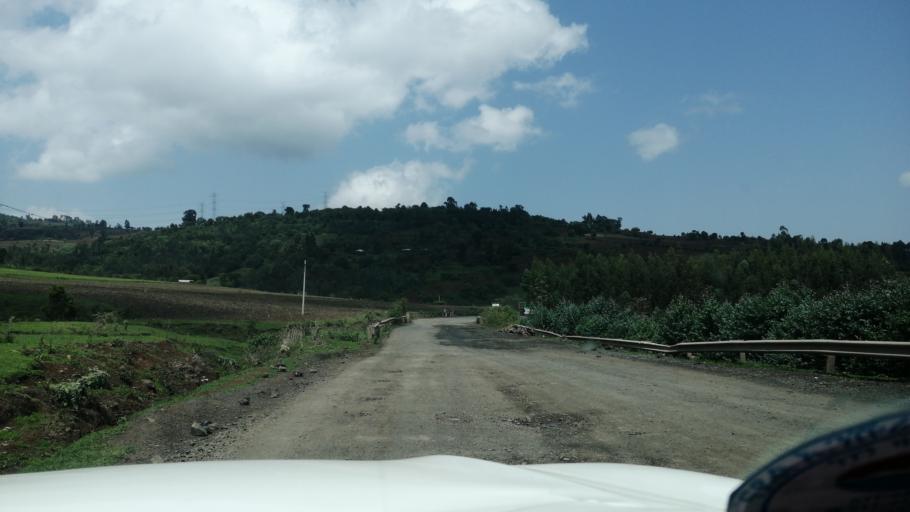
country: ET
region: Oromiya
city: Gedo
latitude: 8.9683
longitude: 37.5798
